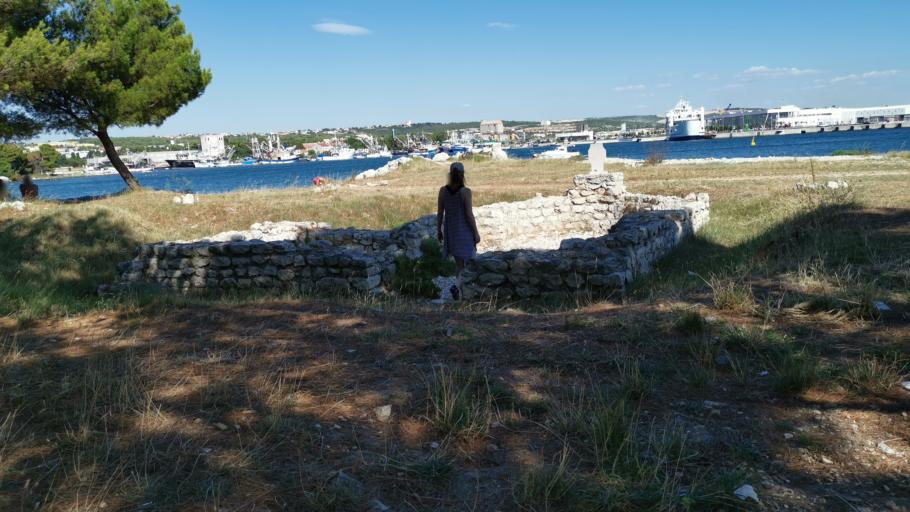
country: HR
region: Zadarska
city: Zadar
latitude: 44.0960
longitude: 15.2525
